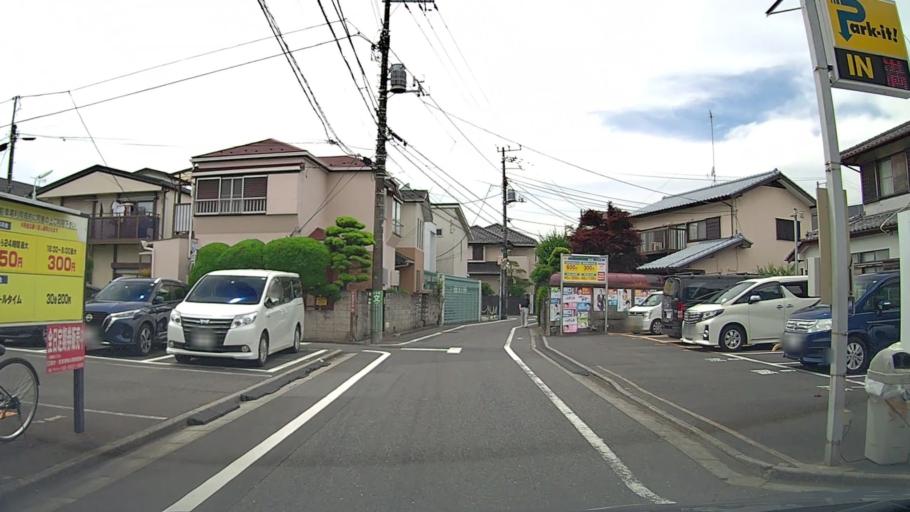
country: JP
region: Tokyo
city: Musashino
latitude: 35.7145
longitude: 139.6234
